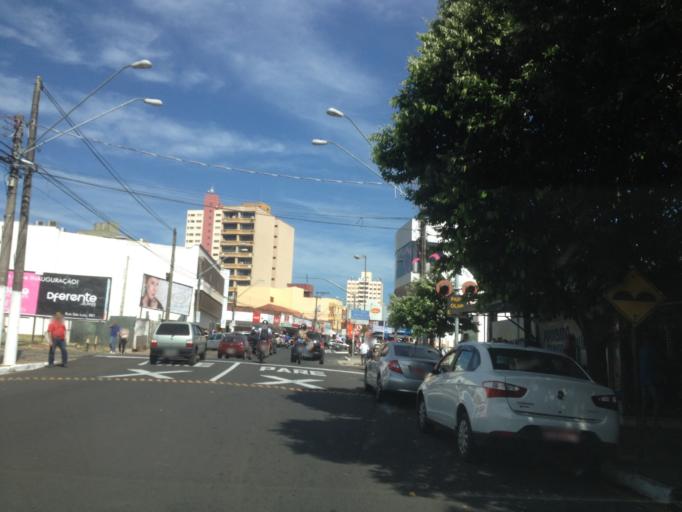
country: BR
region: Sao Paulo
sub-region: Marilia
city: Marilia
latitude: -22.2168
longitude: -49.9463
